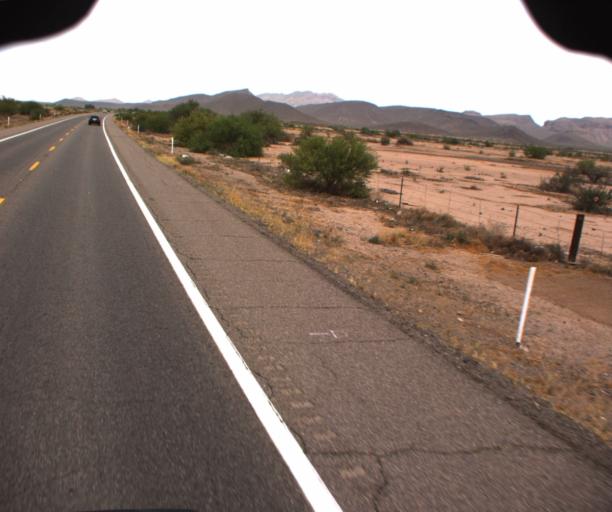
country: US
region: Arizona
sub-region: Pinal County
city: Sacaton
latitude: 33.0794
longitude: -111.7043
